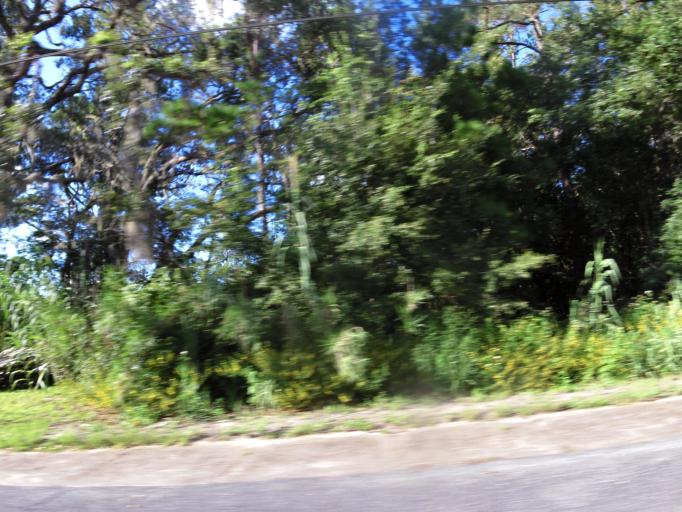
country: US
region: Florida
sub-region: Wakulla County
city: Crawfordville
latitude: 30.0619
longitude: -84.4955
